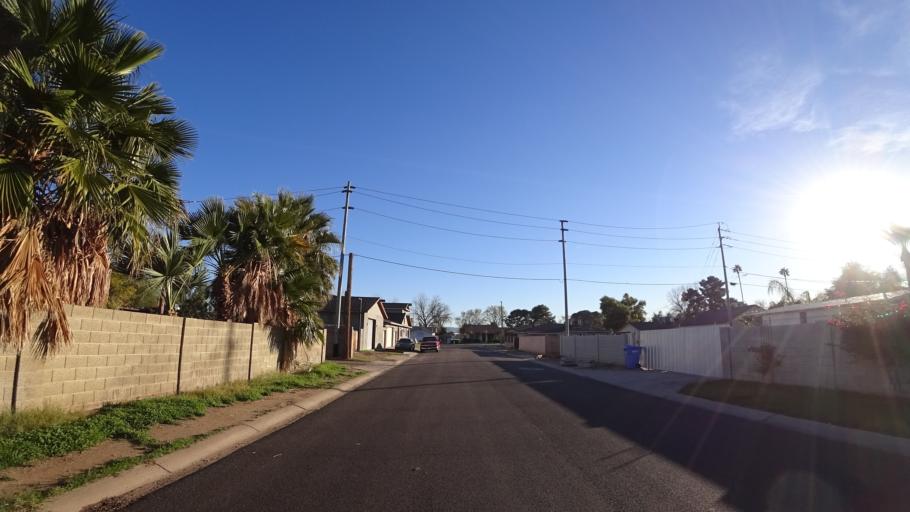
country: US
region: Arizona
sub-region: Maricopa County
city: Phoenix
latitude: 33.4776
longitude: -112.1064
